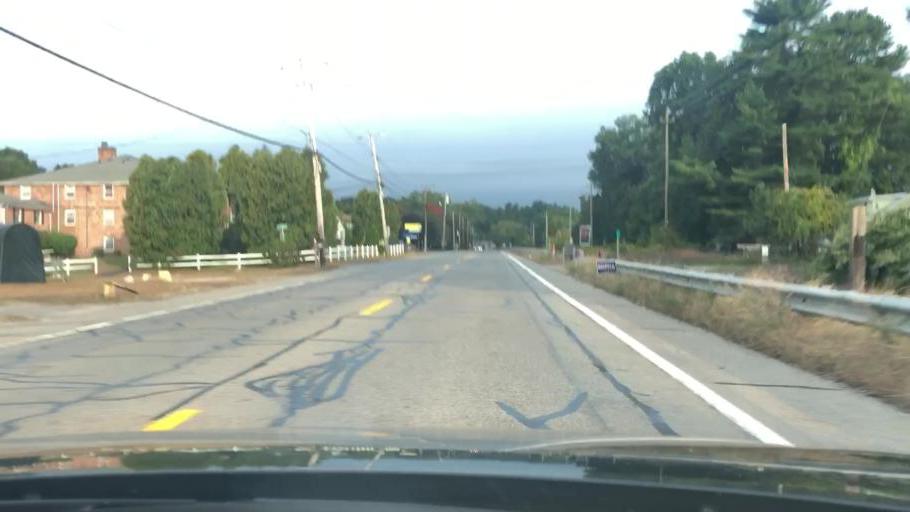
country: US
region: Massachusetts
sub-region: Middlesex County
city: Tyngsboro
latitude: 42.6474
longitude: -71.3958
